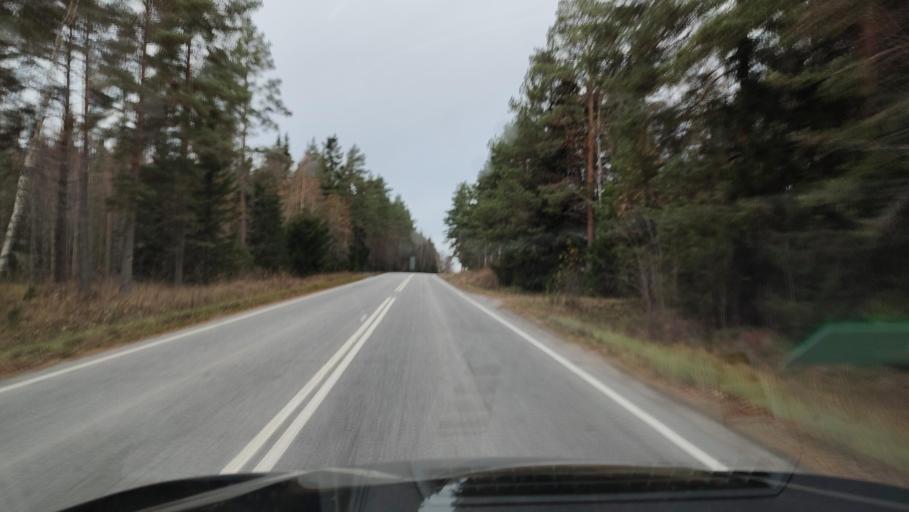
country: FI
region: Ostrobothnia
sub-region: Sydosterbotten
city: Naerpes
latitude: 62.4009
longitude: 21.3617
